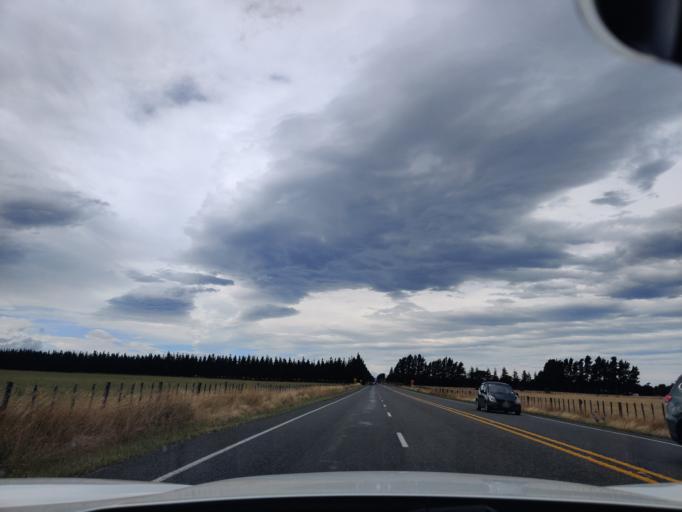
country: NZ
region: Wellington
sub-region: Masterton District
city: Masterton
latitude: -40.9937
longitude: 175.5658
